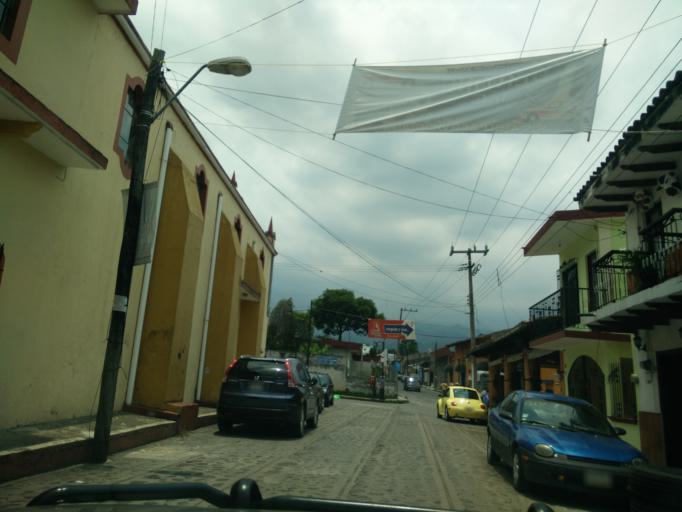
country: MX
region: Veracruz
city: Xico
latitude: 19.4183
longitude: -97.0021
